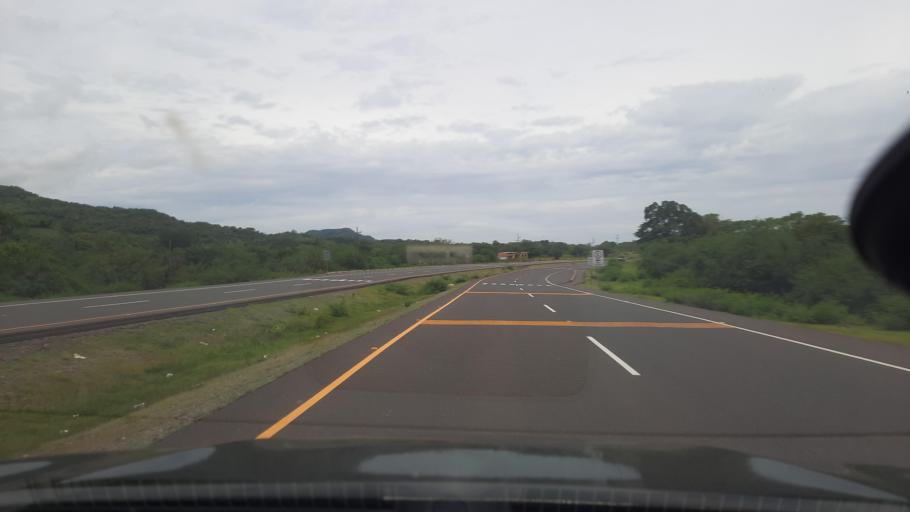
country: HN
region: Valle
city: Aramecina
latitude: 13.7113
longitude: -87.7067
